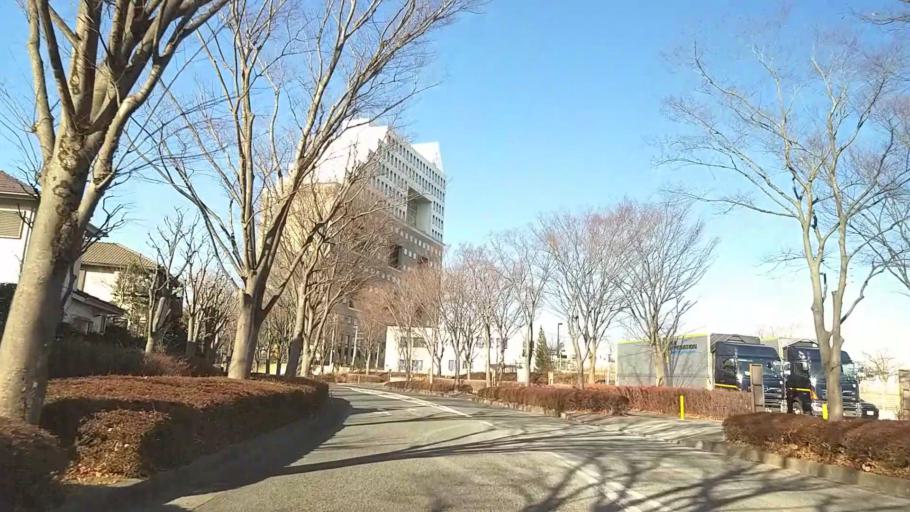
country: JP
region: Kanagawa
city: Atsugi
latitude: 35.4485
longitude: 139.3107
